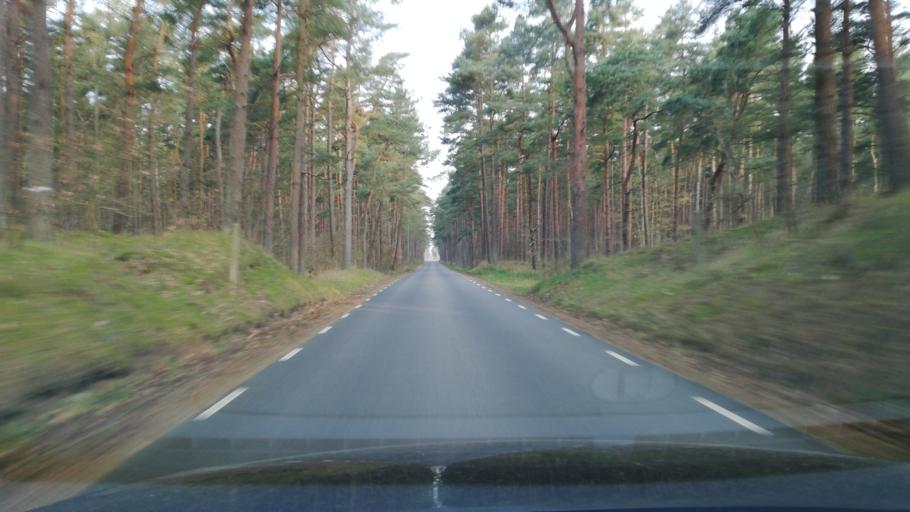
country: SE
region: Skane
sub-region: Simrishamns Kommun
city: Simrishamn
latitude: 55.3908
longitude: 14.1870
